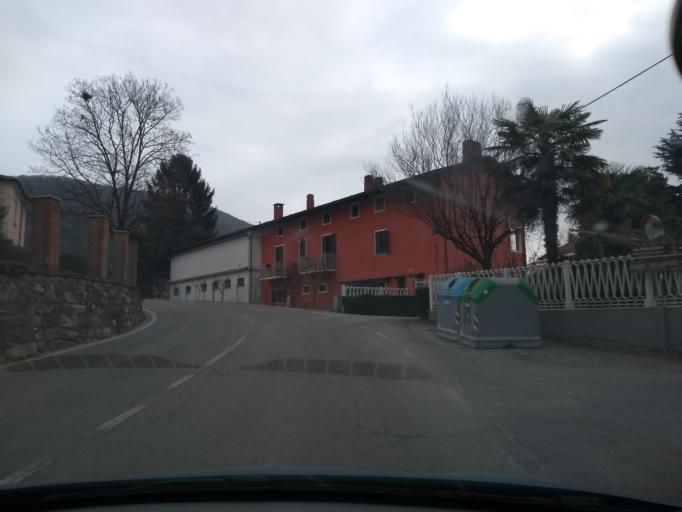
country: IT
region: Piedmont
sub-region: Provincia di Torino
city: Bollengo
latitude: 45.4715
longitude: 7.9550
